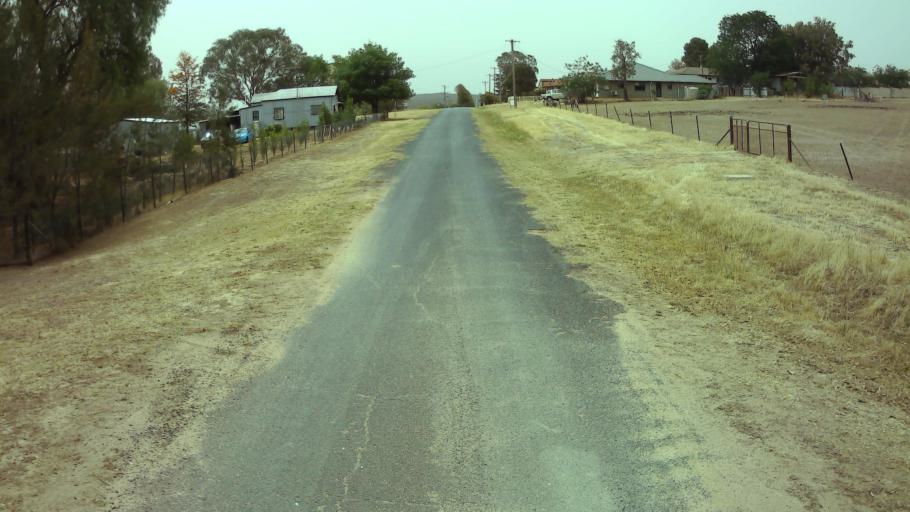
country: AU
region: New South Wales
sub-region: Weddin
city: Grenfell
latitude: -33.9029
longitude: 148.1546
